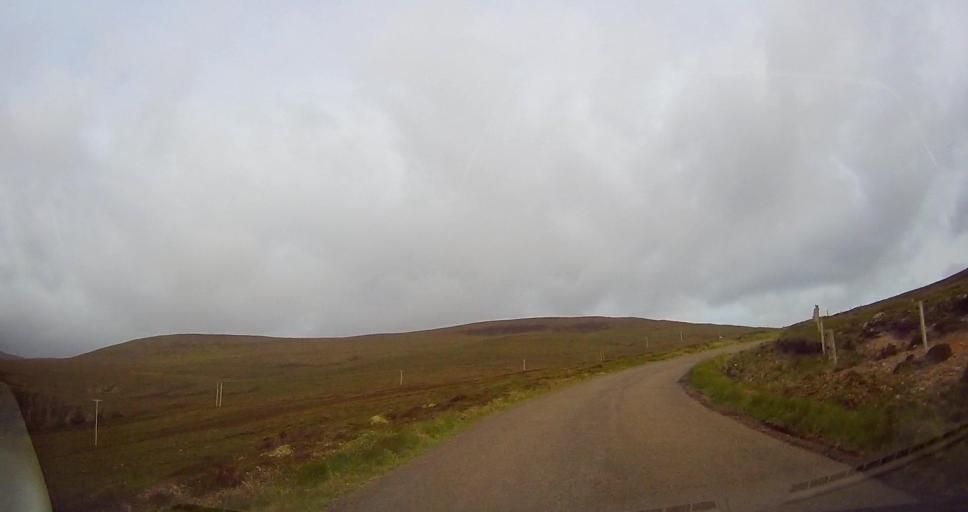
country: GB
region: Scotland
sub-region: Orkney Islands
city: Stromness
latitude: 58.8754
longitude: -3.2462
